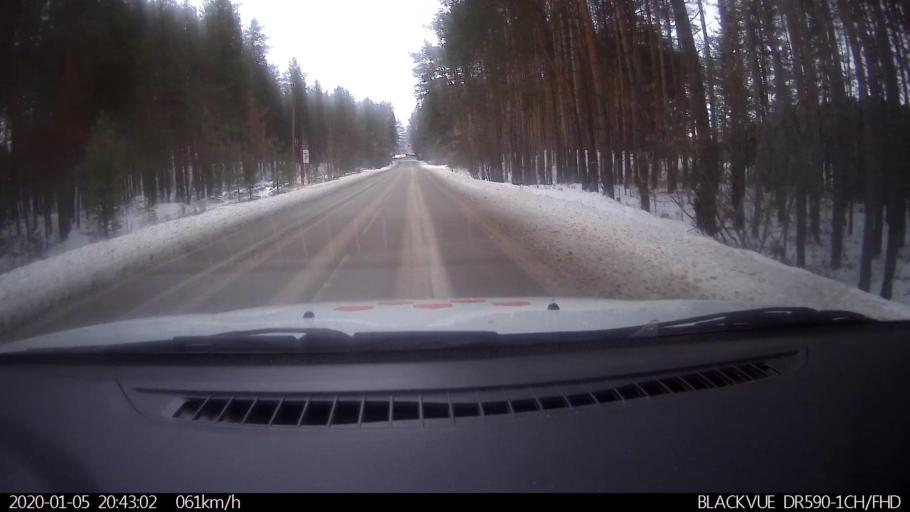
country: RU
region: Nizjnij Novgorod
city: Lukino
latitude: 56.3929
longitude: 43.7365
